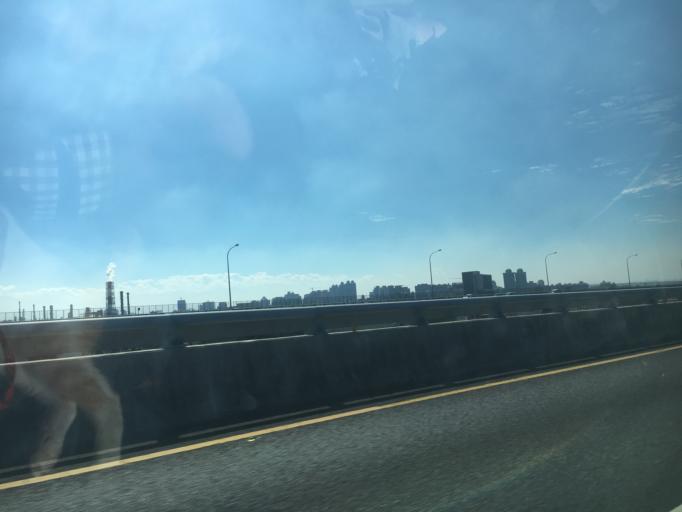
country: TW
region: Taiwan
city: Taoyuan City
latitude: 25.0425
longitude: 121.3056
